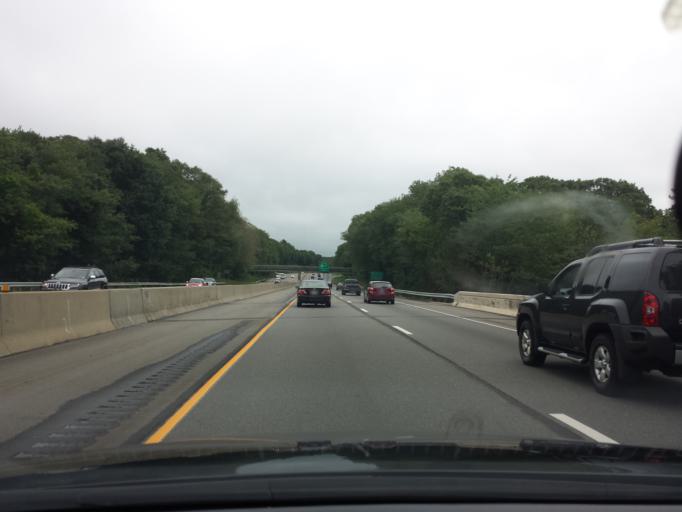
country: US
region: Connecticut
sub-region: Middlesex County
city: Clinton
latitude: 41.2914
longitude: -72.4961
